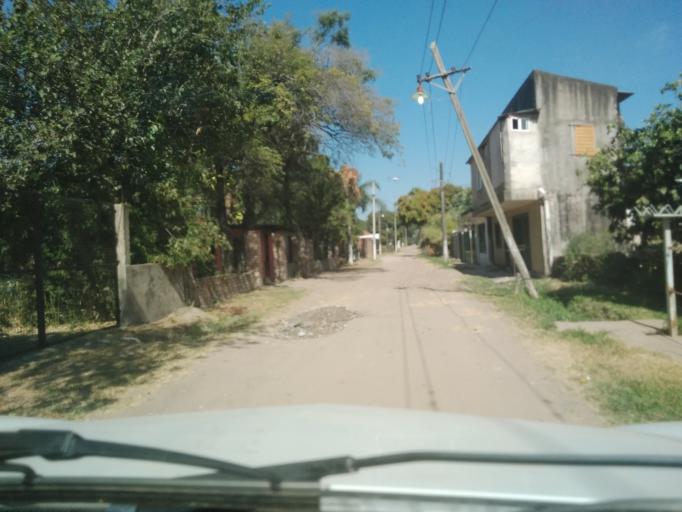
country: AR
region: Corrientes
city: Corrientes
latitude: -27.5131
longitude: -58.8035
